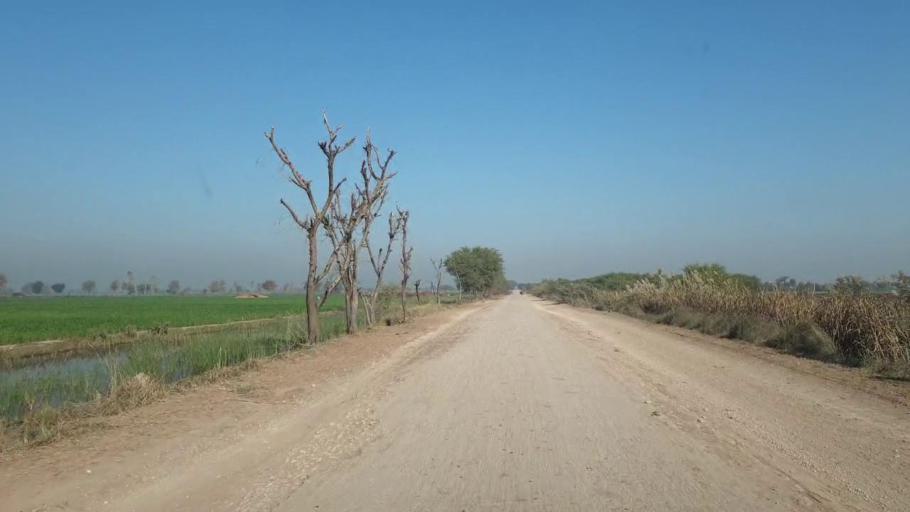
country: PK
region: Sindh
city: Shahdadpur
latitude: 25.9293
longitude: 68.5056
